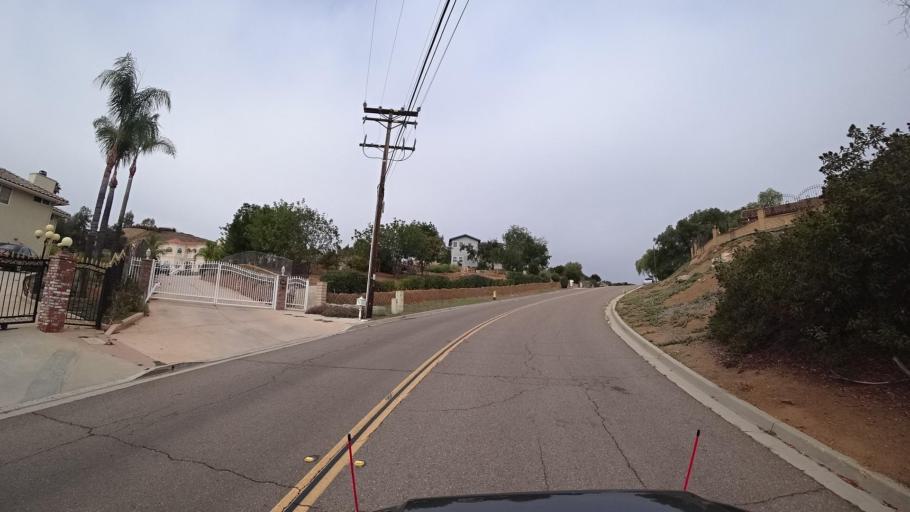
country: US
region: California
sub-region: San Diego County
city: Rancho San Diego
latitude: 32.7644
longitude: -116.9289
